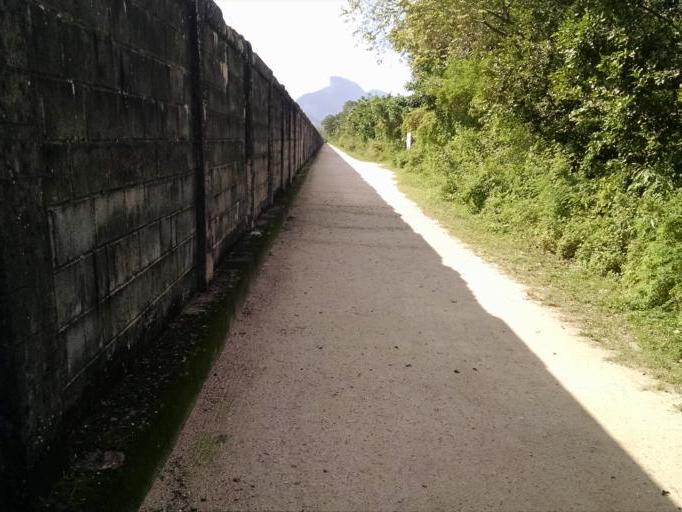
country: BR
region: Rio de Janeiro
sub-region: Sao Joao De Meriti
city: Sao Joao de Meriti
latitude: -22.9934
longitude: -43.3742
